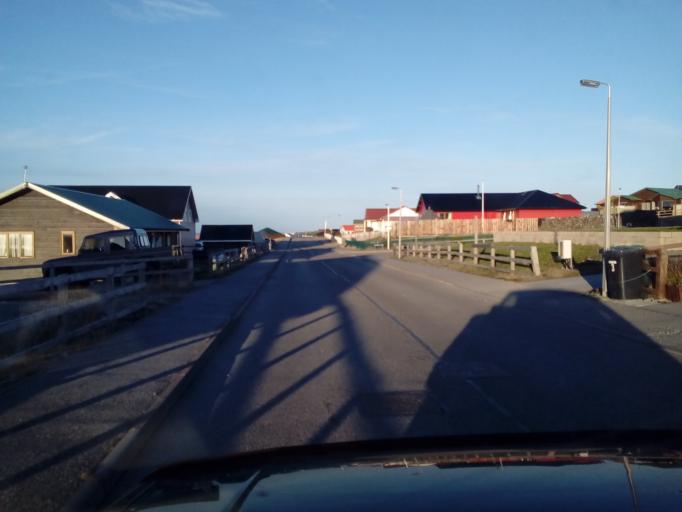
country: FK
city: Stanley
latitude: -51.6956
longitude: -57.8365
